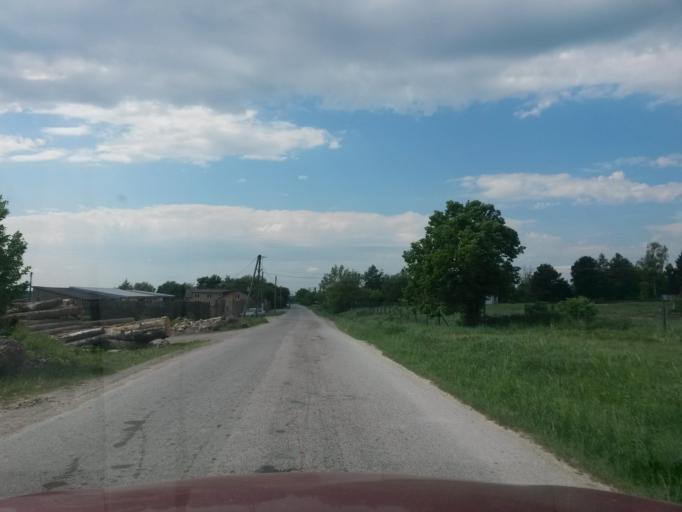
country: SK
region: Kosicky
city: Moldava nad Bodvou
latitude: 48.6982
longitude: 21.0126
